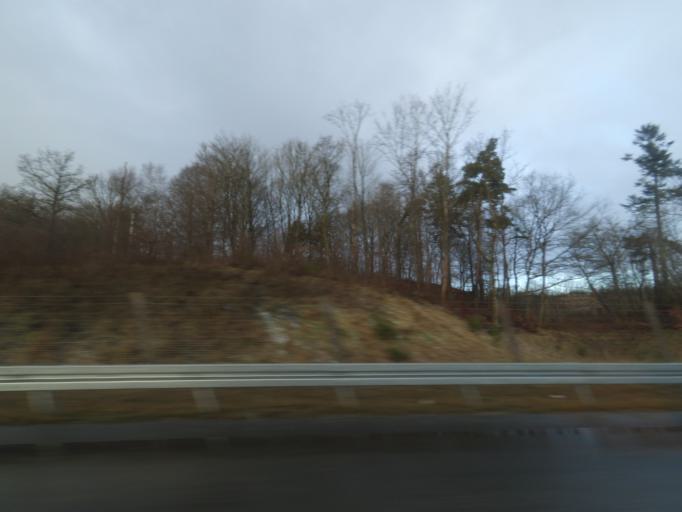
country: DK
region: Central Jutland
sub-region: Silkeborg Kommune
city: Silkeborg
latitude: 56.1762
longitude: 9.4789
